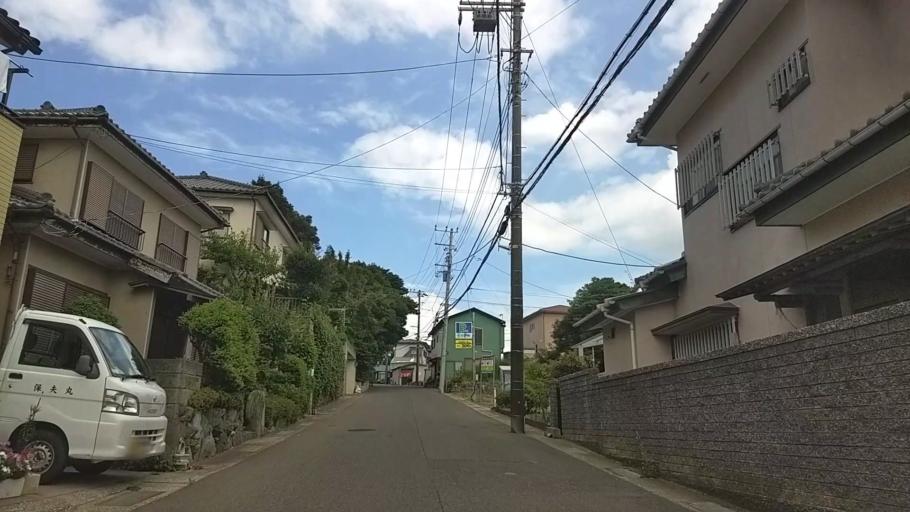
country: JP
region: Kanagawa
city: Miura
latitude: 35.1981
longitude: 139.6078
